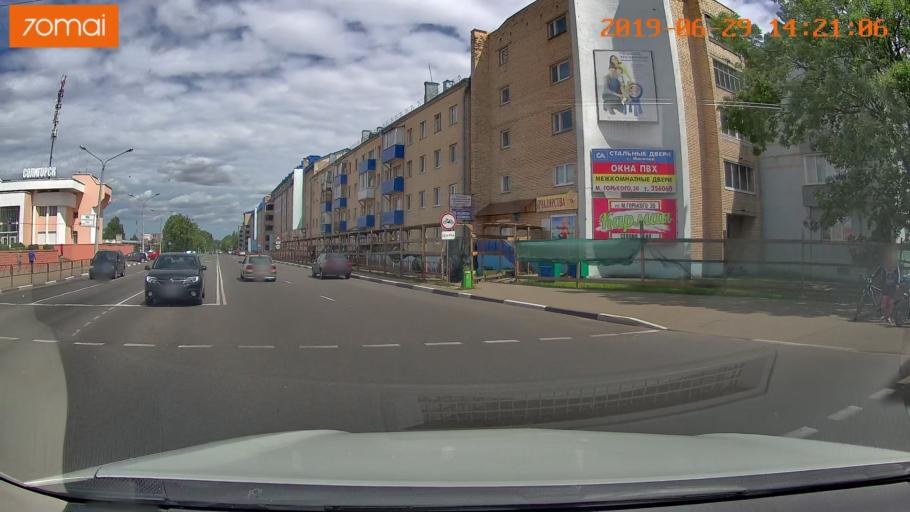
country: BY
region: Minsk
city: Salihorsk
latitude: 52.7922
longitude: 27.5436
